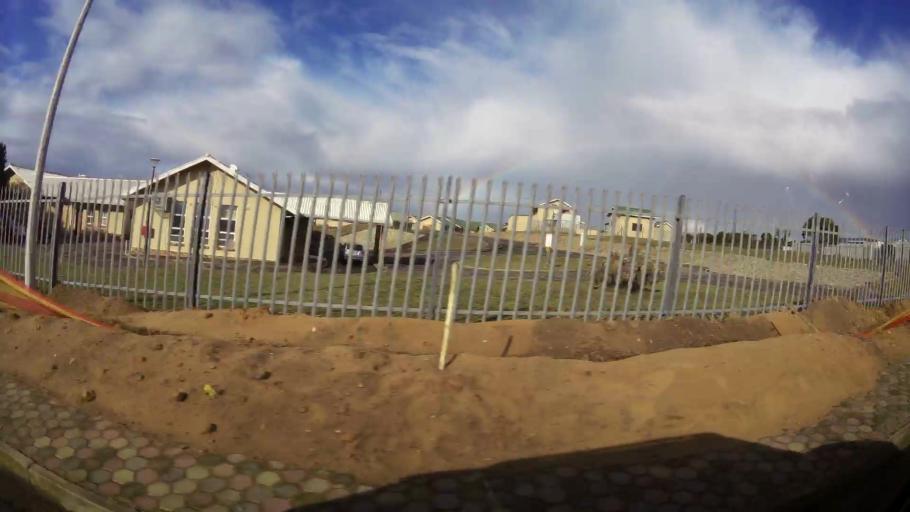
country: ZA
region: Western Cape
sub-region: Eden District Municipality
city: Mossel Bay
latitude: -34.1863
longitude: 22.1270
